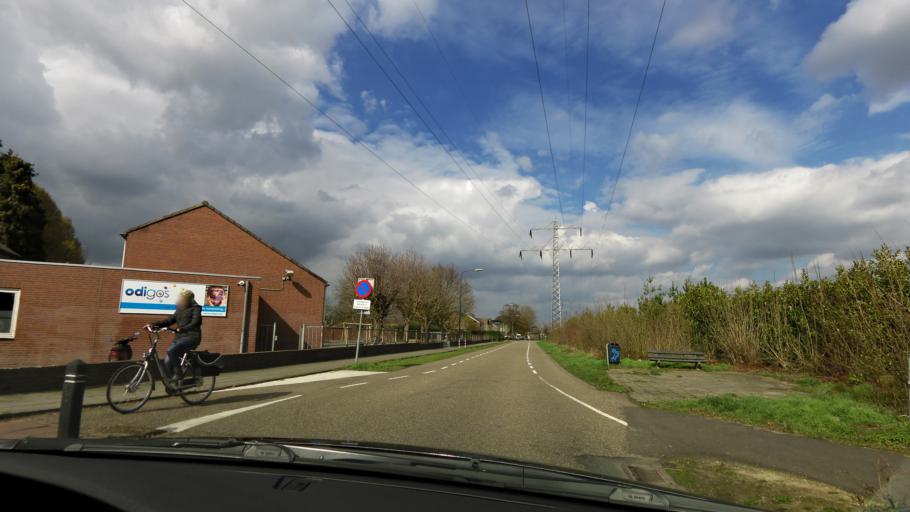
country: NL
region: Limburg
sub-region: Gemeente Sittard-Geleen
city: Limbricht
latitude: 51.0129
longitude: 5.8219
